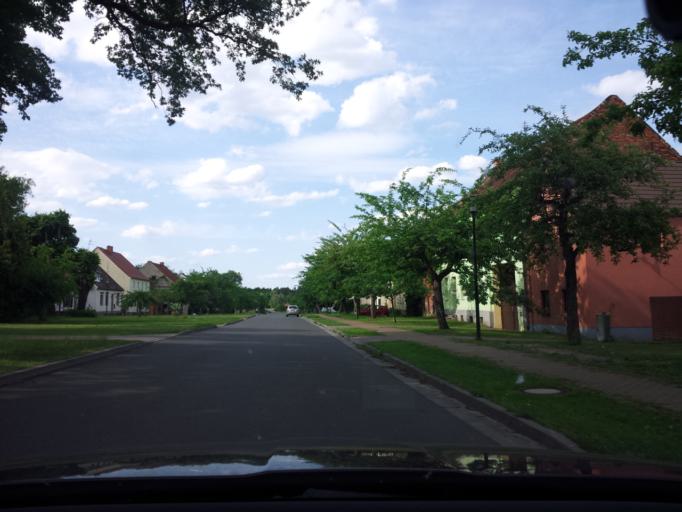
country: DE
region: Brandenburg
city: Juterbog
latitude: 52.0216
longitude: 13.0584
